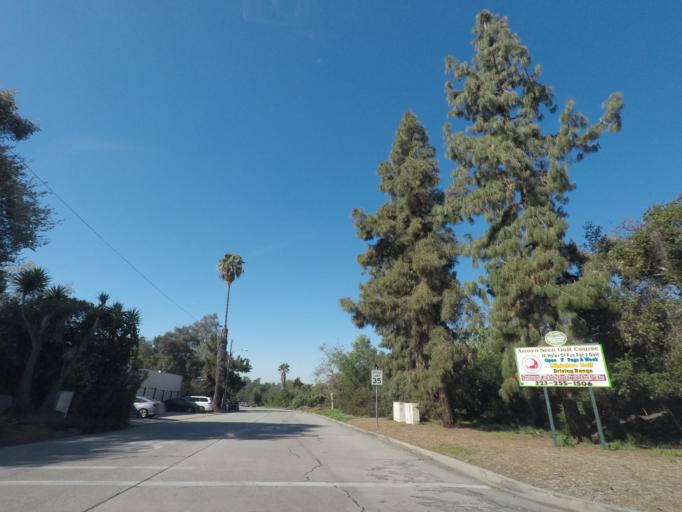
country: US
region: California
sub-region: Los Angeles County
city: South Pasadena
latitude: 34.1157
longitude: -118.1672
